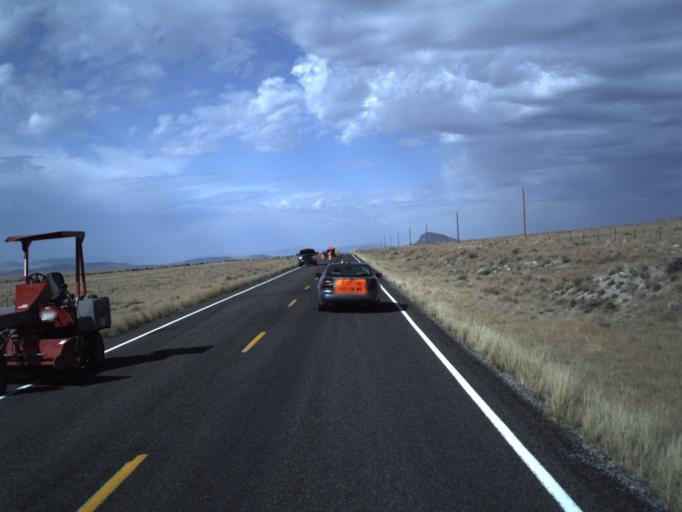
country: US
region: Utah
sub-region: Tooele County
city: Wendover
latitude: 41.4399
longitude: -113.7145
